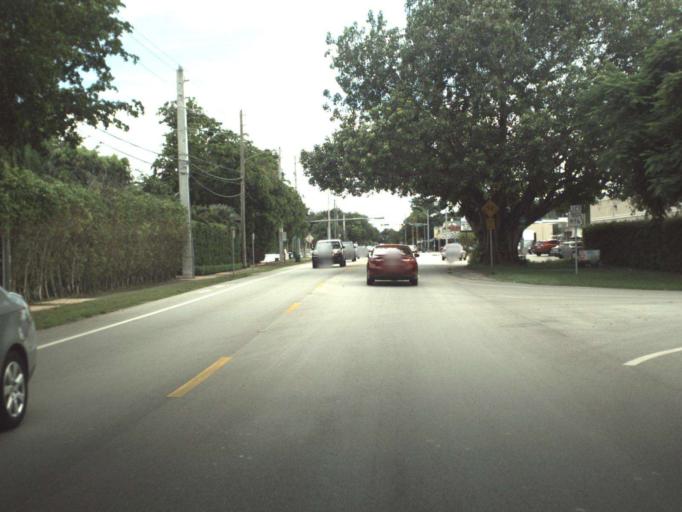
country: US
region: Florida
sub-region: Miami-Dade County
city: Coral Terrace
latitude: 25.7357
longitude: -80.2866
